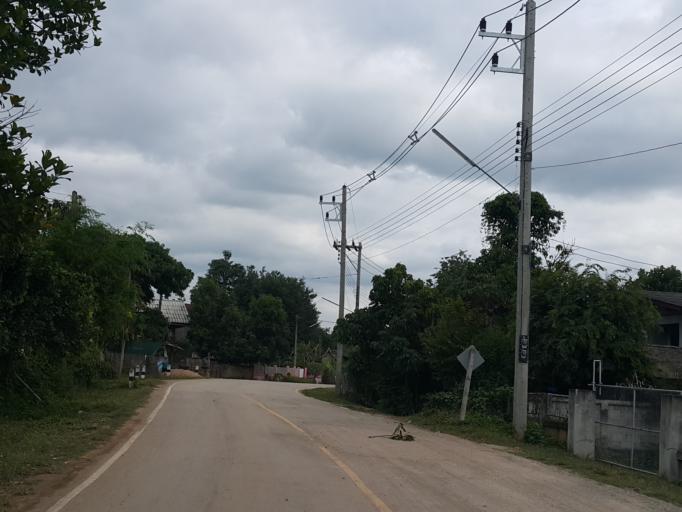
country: TH
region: Lampang
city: Chae Hom
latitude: 18.5748
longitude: 99.4539
